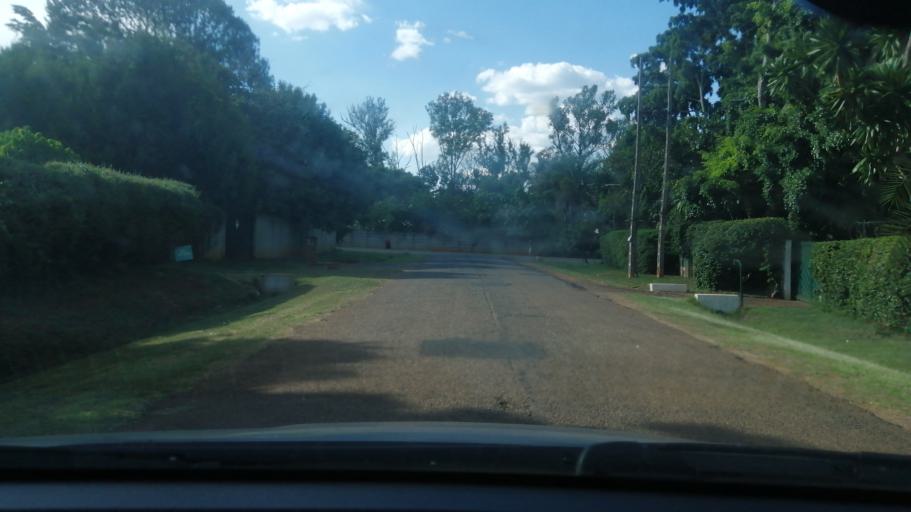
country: ZW
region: Harare
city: Harare
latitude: -17.7653
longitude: 31.0603
